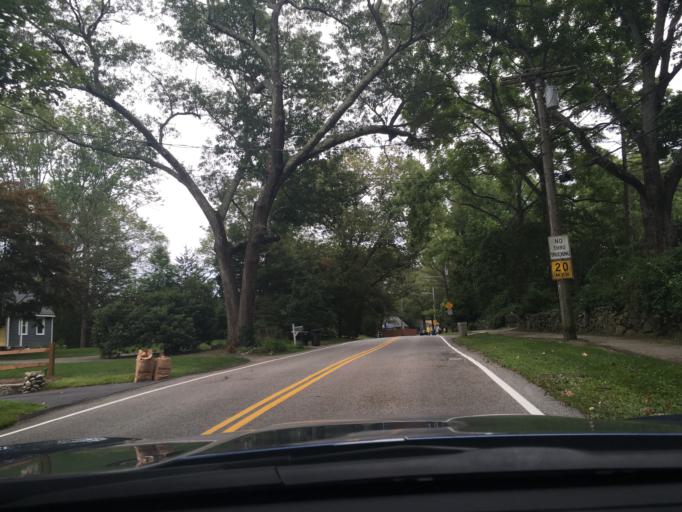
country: US
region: Rhode Island
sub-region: Kent County
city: East Greenwich
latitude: 41.6549
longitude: -71.4641
